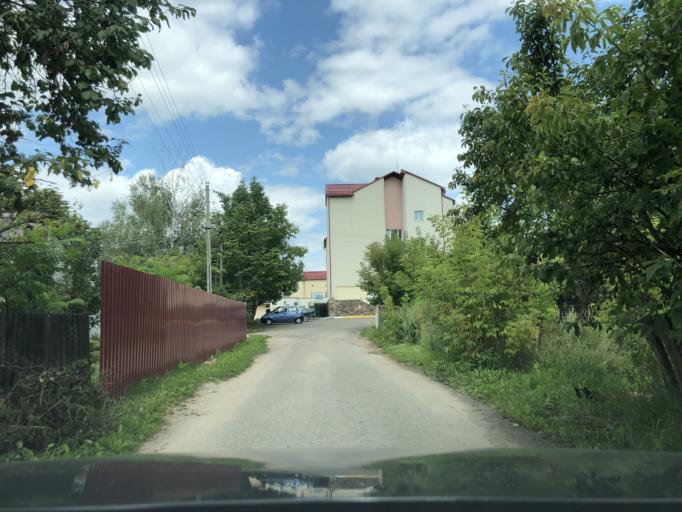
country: BY
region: Minsk
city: Lahoysk
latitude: 54.2048
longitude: 27.8518
